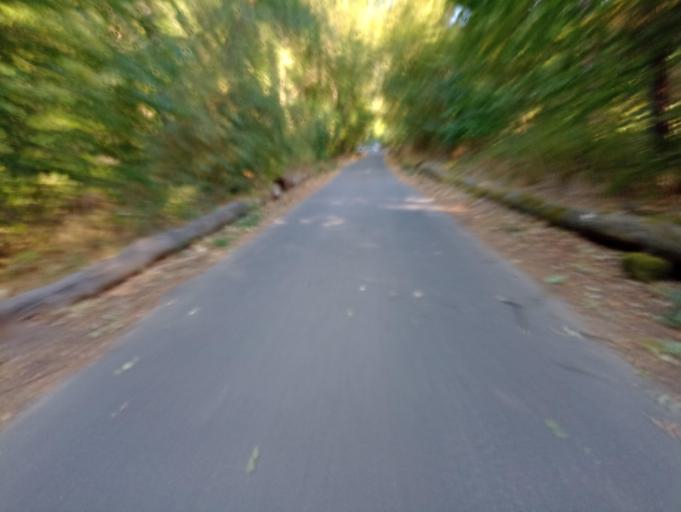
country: DE
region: Hesse
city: Niederrad
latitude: 50.0662
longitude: 8.6290
